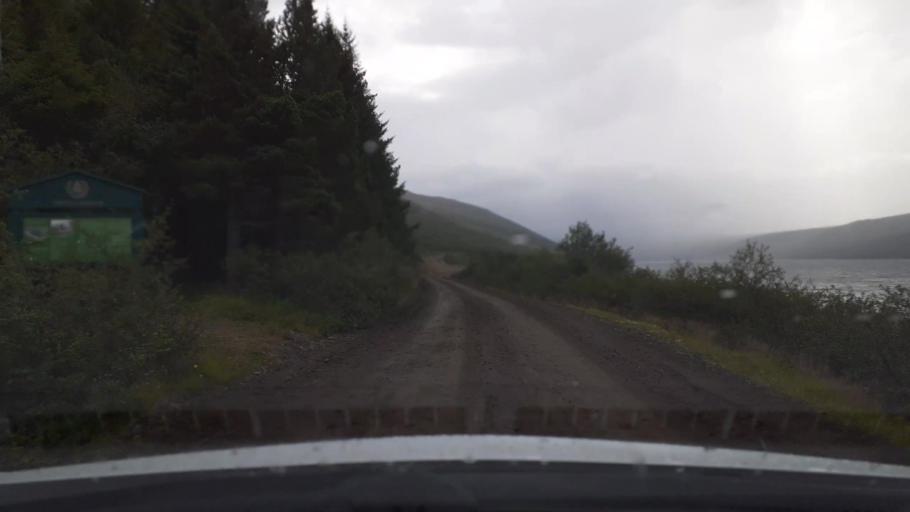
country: IS
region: Capital Region
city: Mosfellsbaer
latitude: 64.5100
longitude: -21.3932
